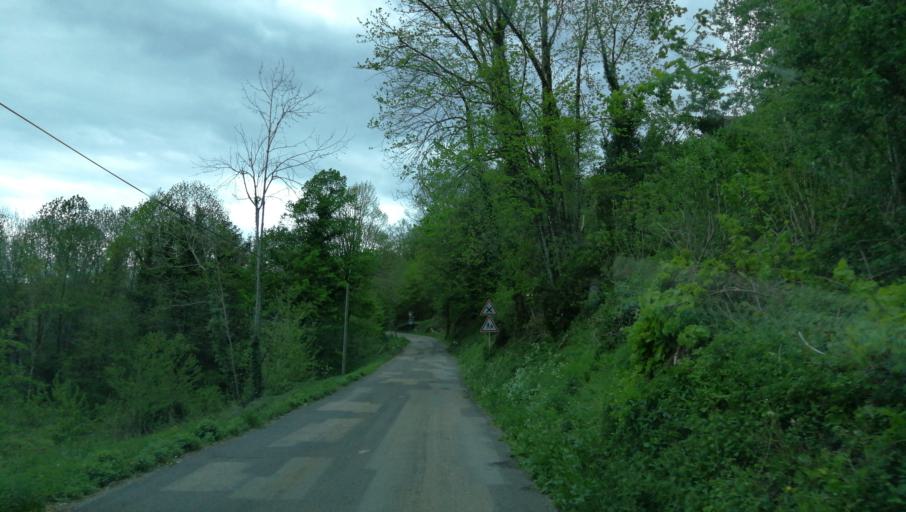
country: FR
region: Rhone-Alpes
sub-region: Departement de la Savoie
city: Brison-Saint-Innocent
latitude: 45.7187
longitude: 5.8506
